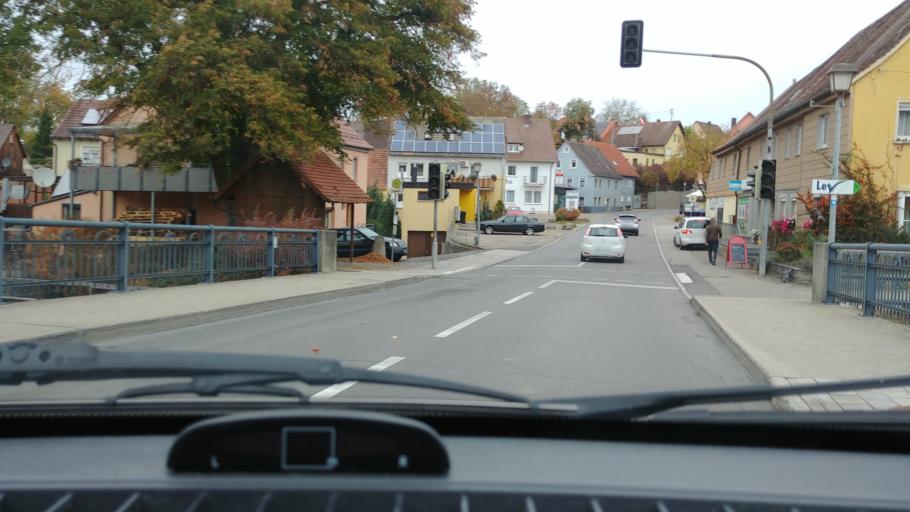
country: DE
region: Baden-Wuerttemberg
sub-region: Regierungsbezirk Stuttgart
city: Wallhausen
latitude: 49.2104
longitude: 10.0622
